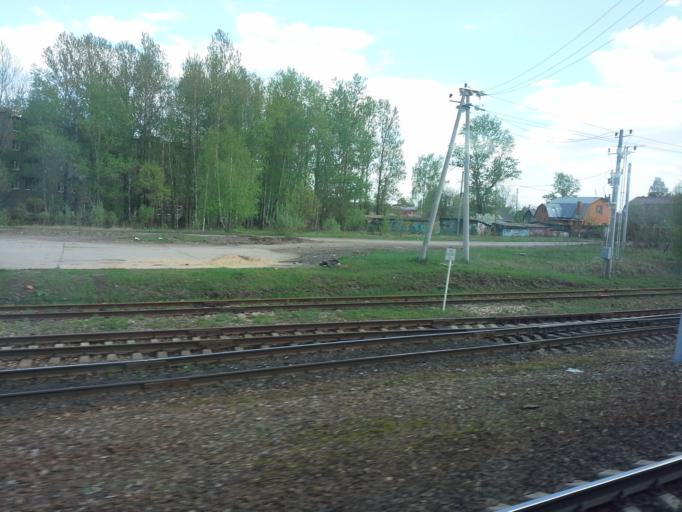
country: RU
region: Moskovskaya
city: Sofrino
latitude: 56.1455
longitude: 37.9366
